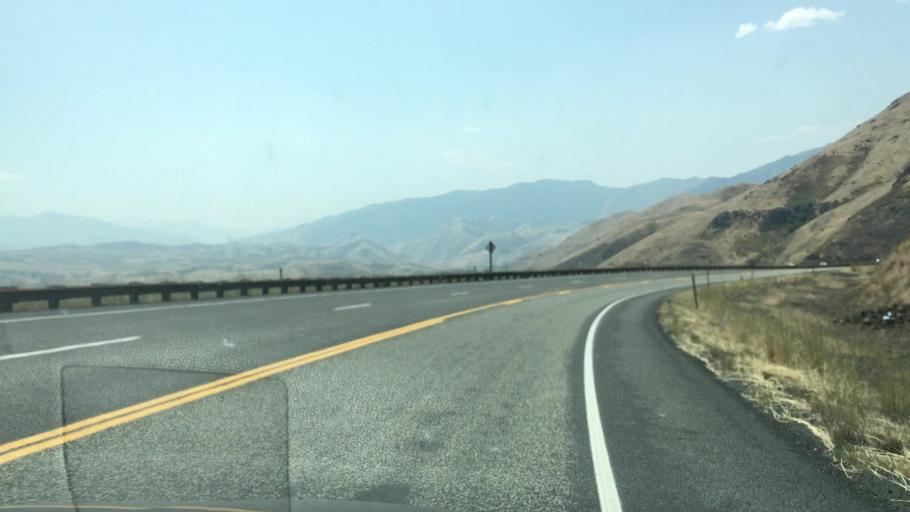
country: US
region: Idaho
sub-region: Idaho County
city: Grangeville
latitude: 45.8072
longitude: -116.2813
